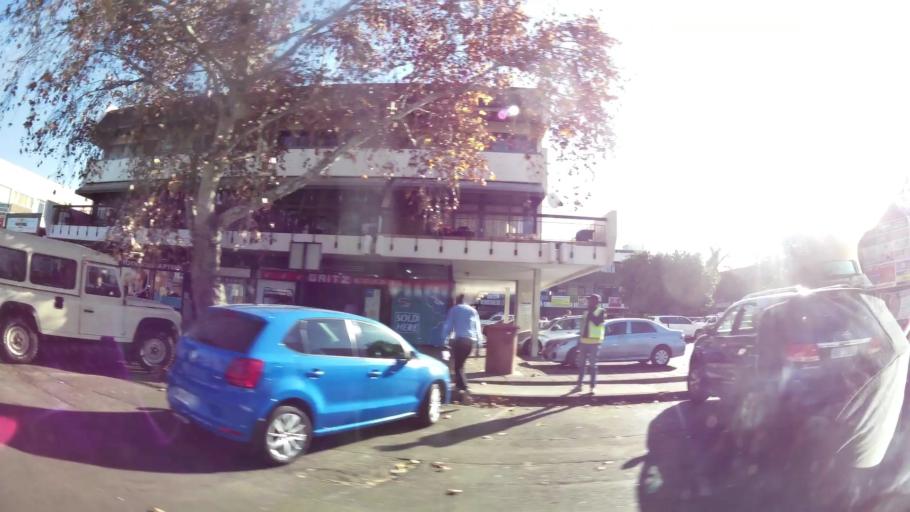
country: ZA
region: Gauteng
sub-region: City of Tshwane Metropolitan Municipality
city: Pretoria
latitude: -25.7029
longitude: 28.2428
